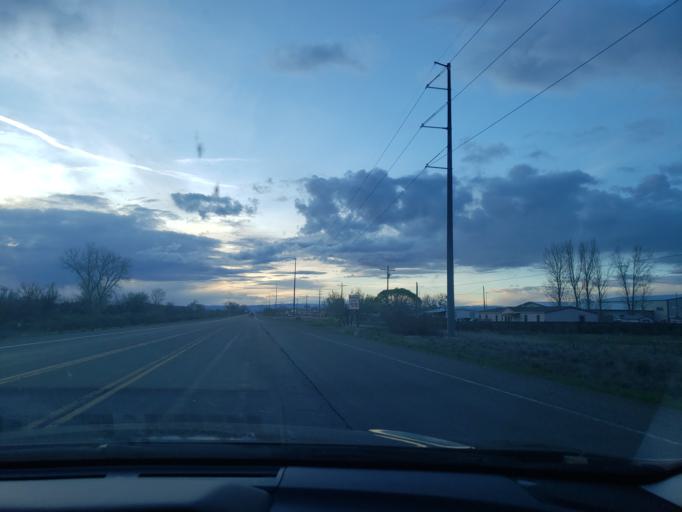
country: US
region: Colorado
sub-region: Mesa County
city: Fruita
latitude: 39.1304
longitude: -108.6843
